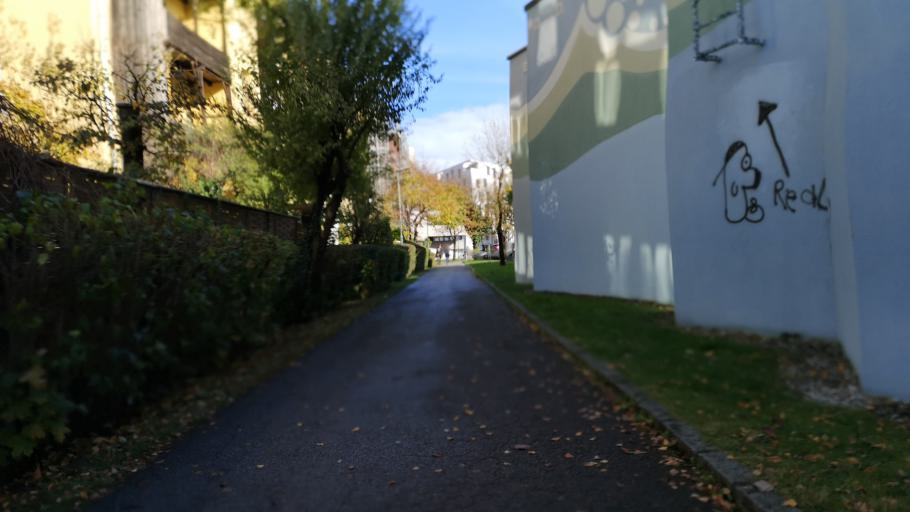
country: AT
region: Tyrol
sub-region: Innsbruck Stadt
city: Innsbruck
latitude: 47.2654
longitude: 11.3806
